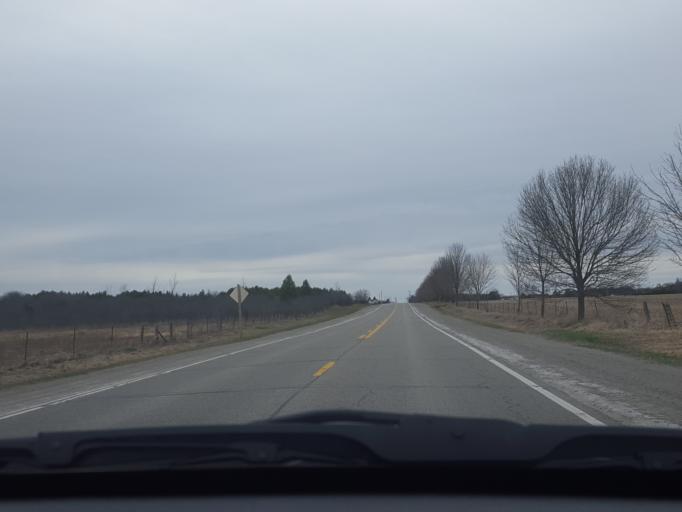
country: CA
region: Ontario
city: Uxbridge
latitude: 44.3099
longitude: -79.1767
